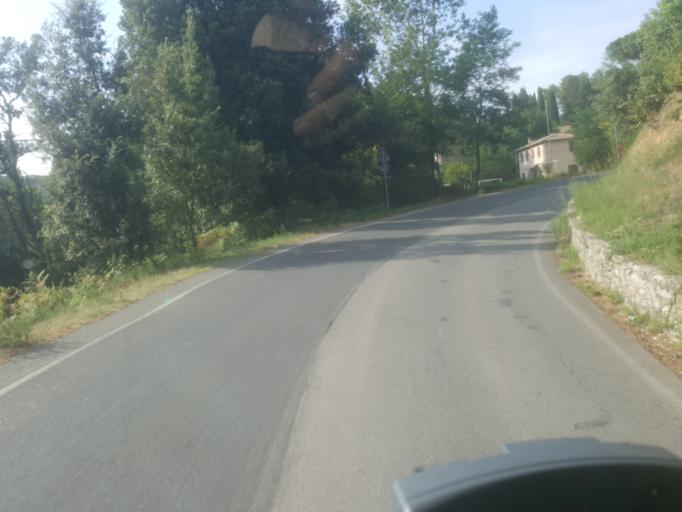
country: IT
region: Tuscany
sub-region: Province of Florence
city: Gambassi Terme
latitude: 43.4909
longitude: 10.9292
